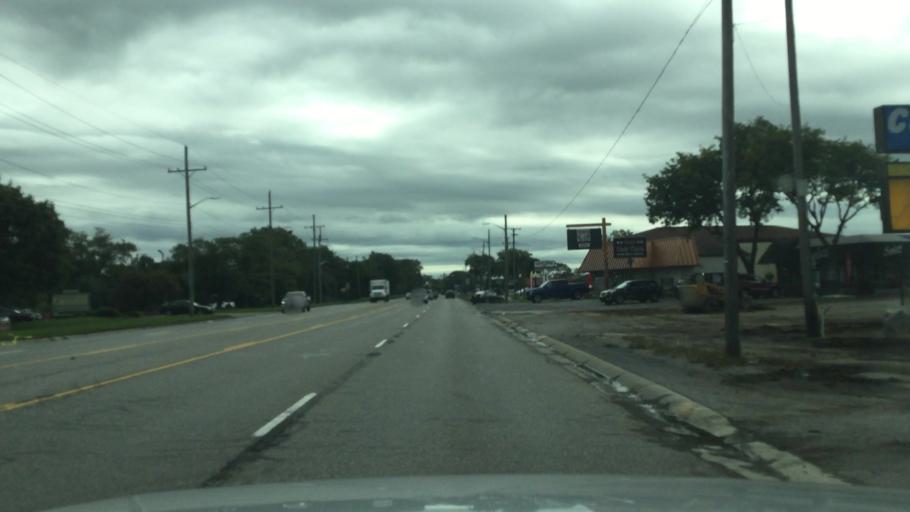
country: US
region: Michigan
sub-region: Oakland County
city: Waterford
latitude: 42.6592
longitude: -83.3832
